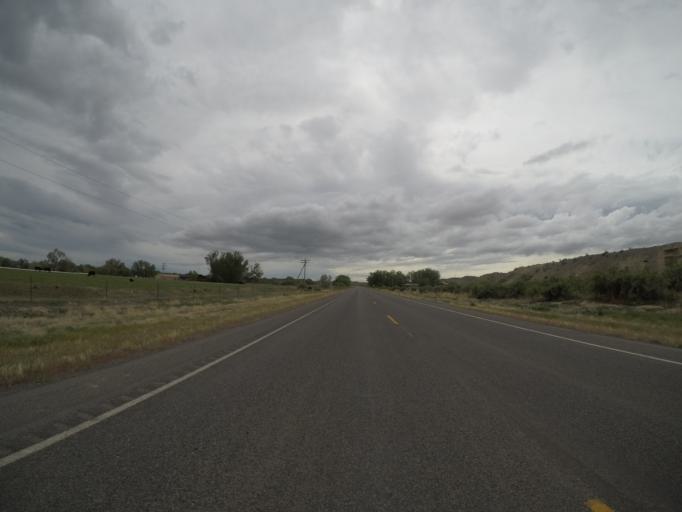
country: US
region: Wyoming
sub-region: Big Horn County
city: Lovell
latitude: 44.8690
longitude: -108.3226
